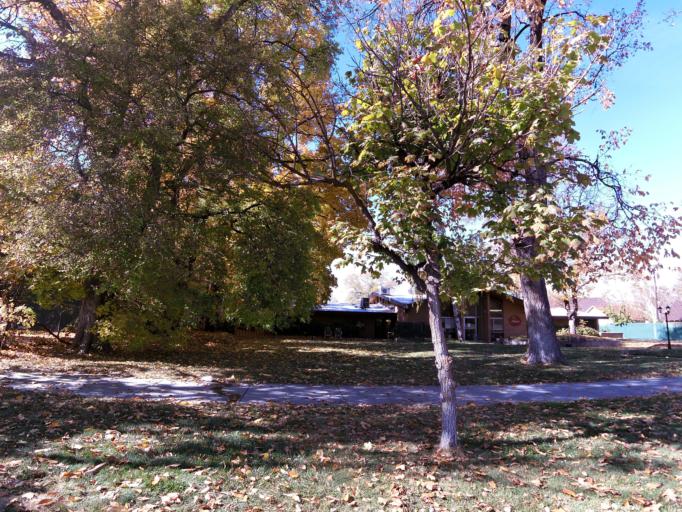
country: US
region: Utah
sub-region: Weber County
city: Ogden
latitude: 41.2239
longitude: -111.9621
